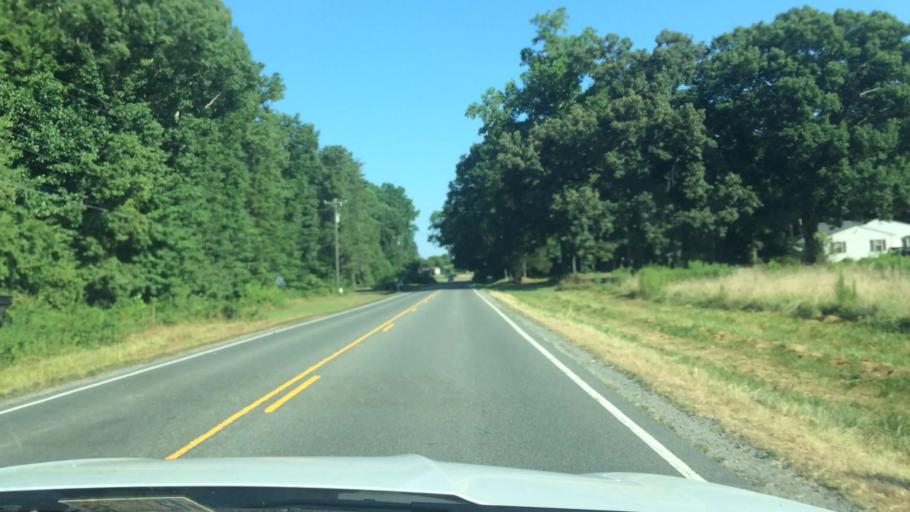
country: US
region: Virginia
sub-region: Lancaster County
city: Lancaster
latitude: 37.7721
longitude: -76.5094
